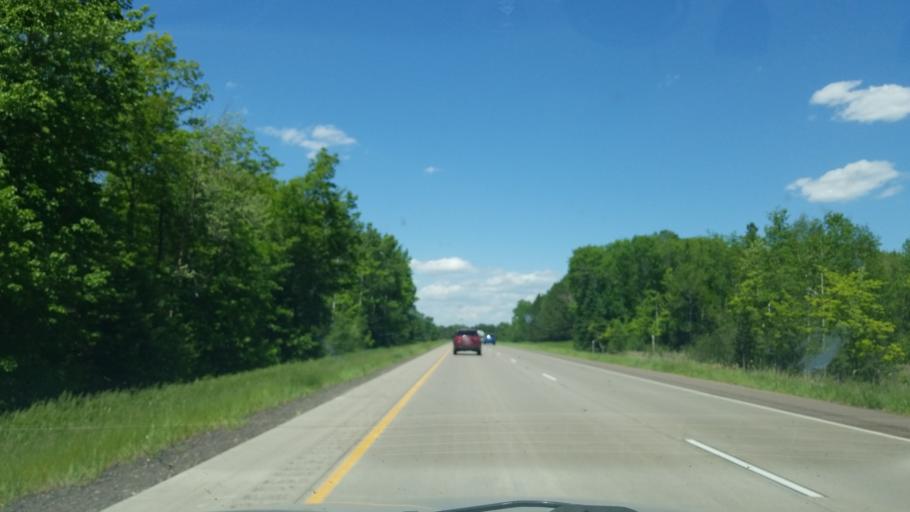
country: US
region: Minnesota
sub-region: Pine County
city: Sandstone
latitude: 46.2288
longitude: -92.8270
